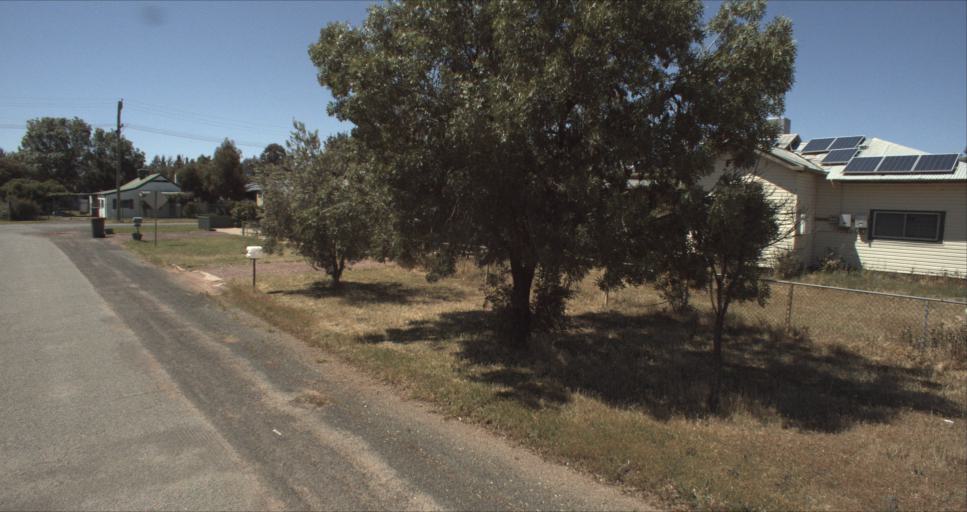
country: AU
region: New South Wales
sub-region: Leeton
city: Leeton
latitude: -34.5240
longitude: 146.3312
